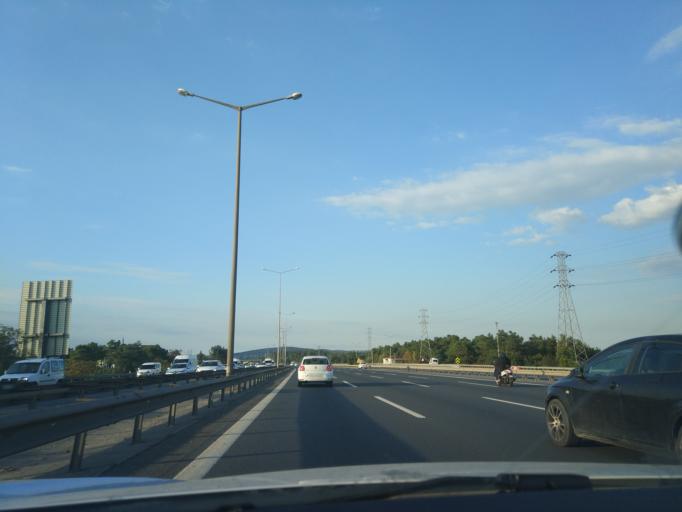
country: TR
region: Istanbul
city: Umraniye
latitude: 41.0455
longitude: 29.1214
